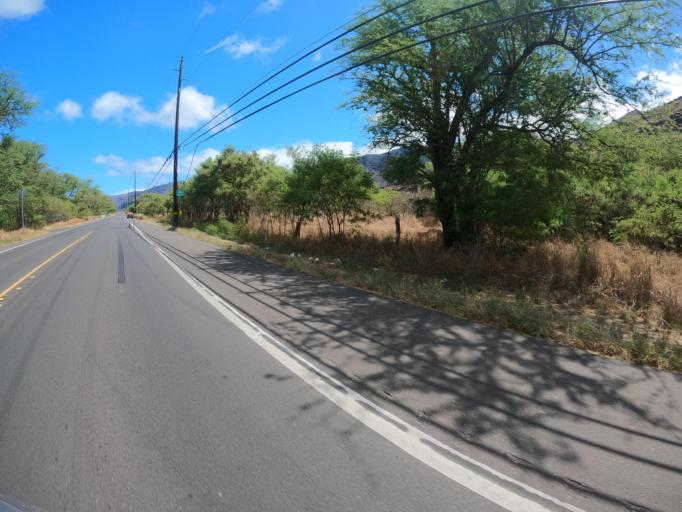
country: US
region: Hawaii
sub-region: Honolulu County
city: Makaha
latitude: 21.4945
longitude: -158.2276
